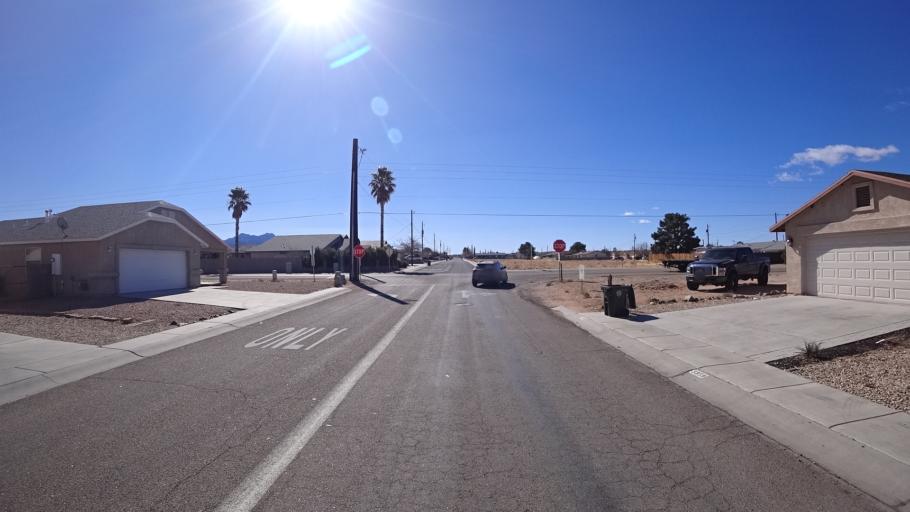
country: US
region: Arizona
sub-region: Mohave County
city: New Kingman-Butler
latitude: 35.2214
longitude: -113.9993
